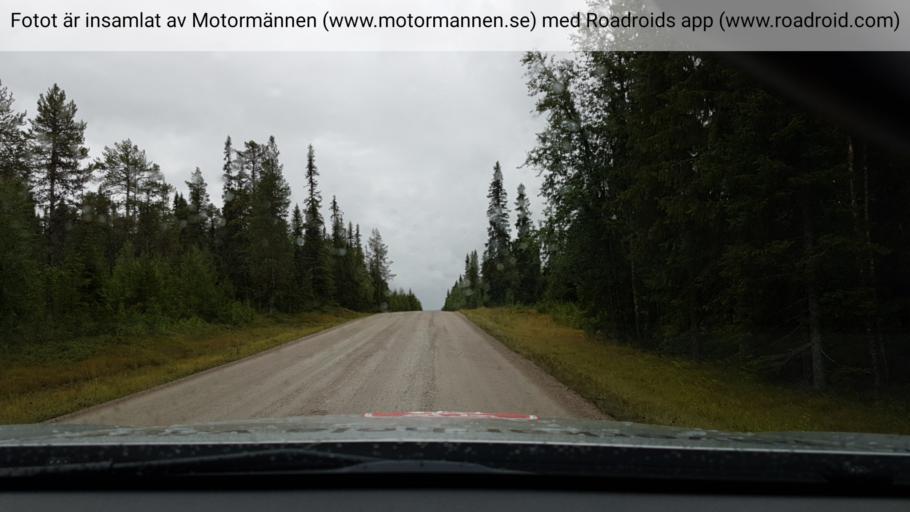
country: SE
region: Vaesterbotten
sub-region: Asele Kommun
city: Insjon
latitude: 64.7347
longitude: 17.6545
